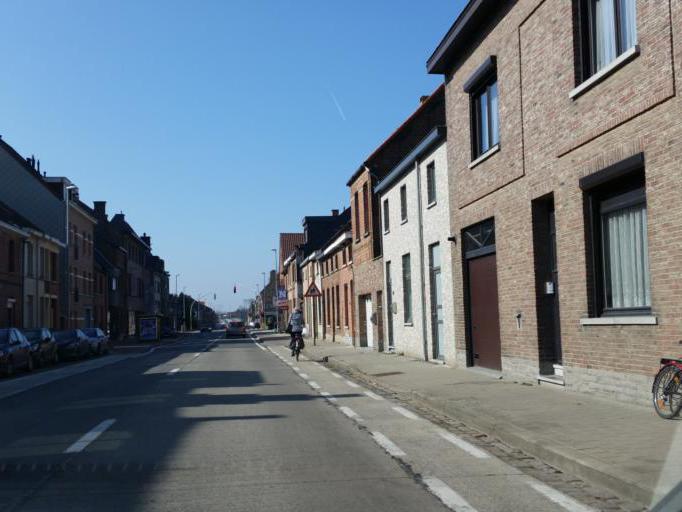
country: BE
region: Flanders
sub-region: Provincie Oost-Vlaanderen
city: Temse
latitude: 51.1289
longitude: 4.2313
